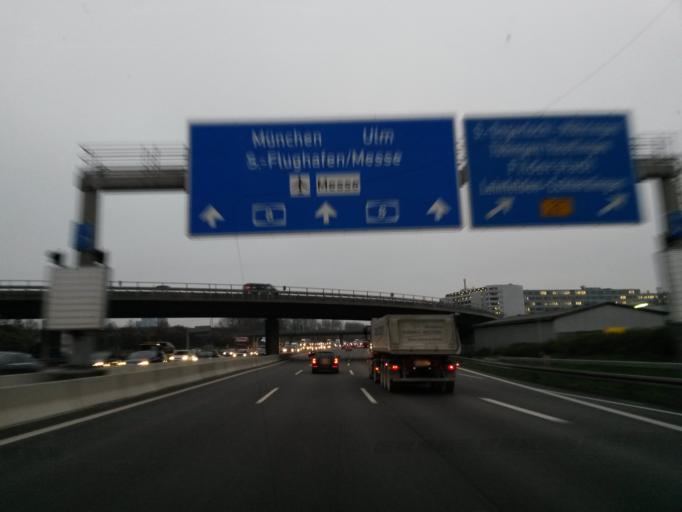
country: DE
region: Baden-Wuerttemberg
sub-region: Regierungsbezirk Stuttgart
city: Leinfelden-Echterdingen
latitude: 48.7096
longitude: 9.1387
